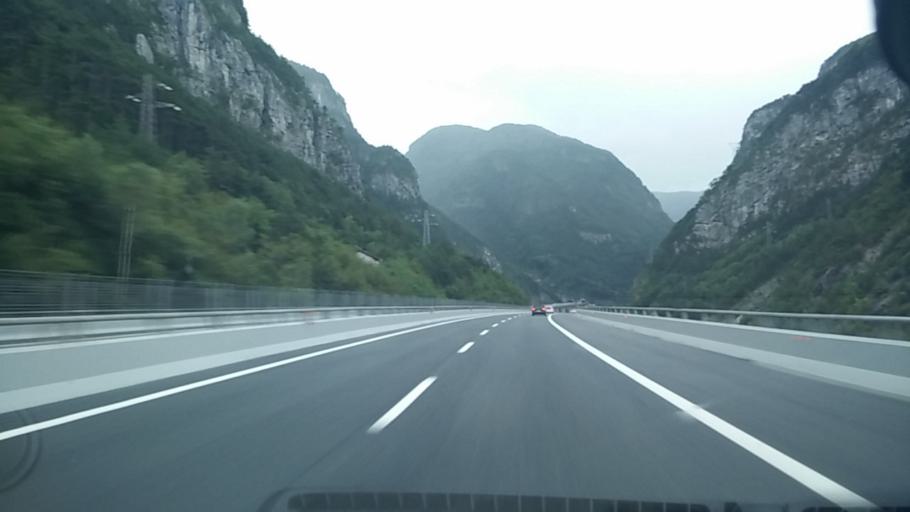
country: IT
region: Friuli Venezia Giulia
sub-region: Provincia di Udine
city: Dogna
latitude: 46.4321
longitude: 13.3146
